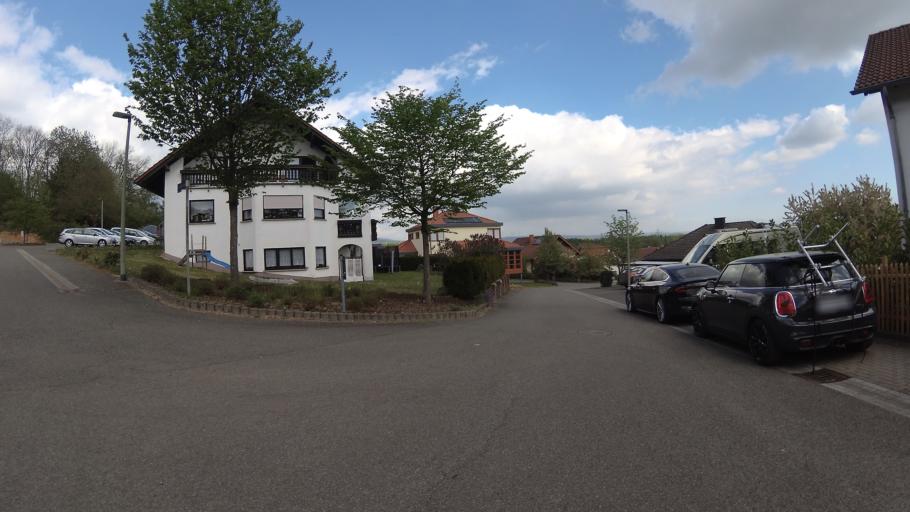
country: DE
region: Saarland
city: Wadern
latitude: 49.5252
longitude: 6.8576
